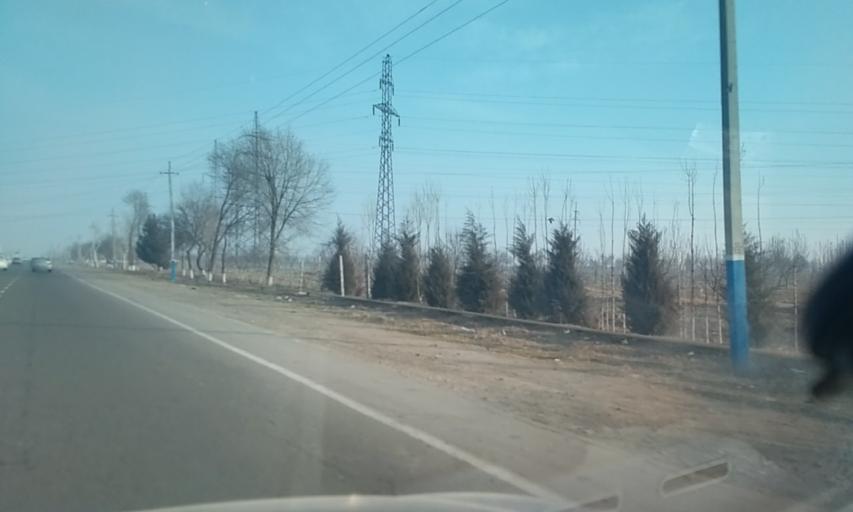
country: UZ
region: Sirdaryo
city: Sirdaryo
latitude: 40.8745
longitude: 68.6692
